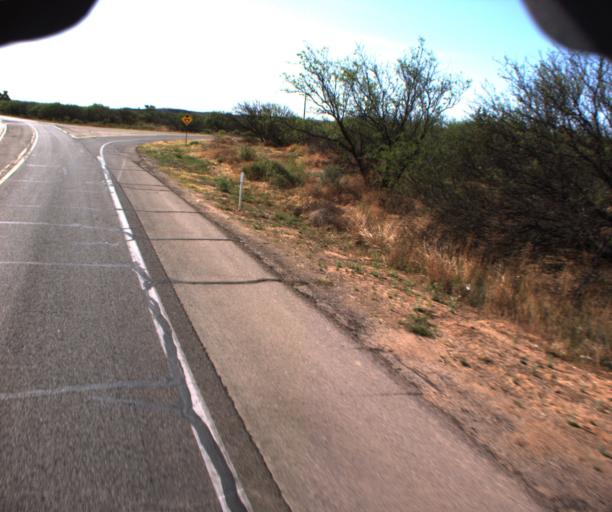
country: US
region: Arizona
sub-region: Cochise County
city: Saint David
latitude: 31.9072
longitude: -110.2552
